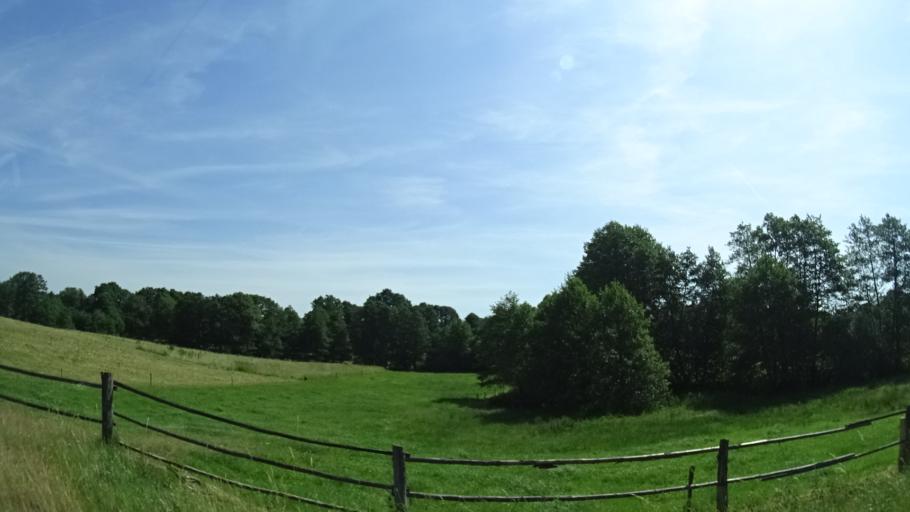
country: DE
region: Hesse
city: Rosenthal
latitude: 50.9238
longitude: 8.8444
